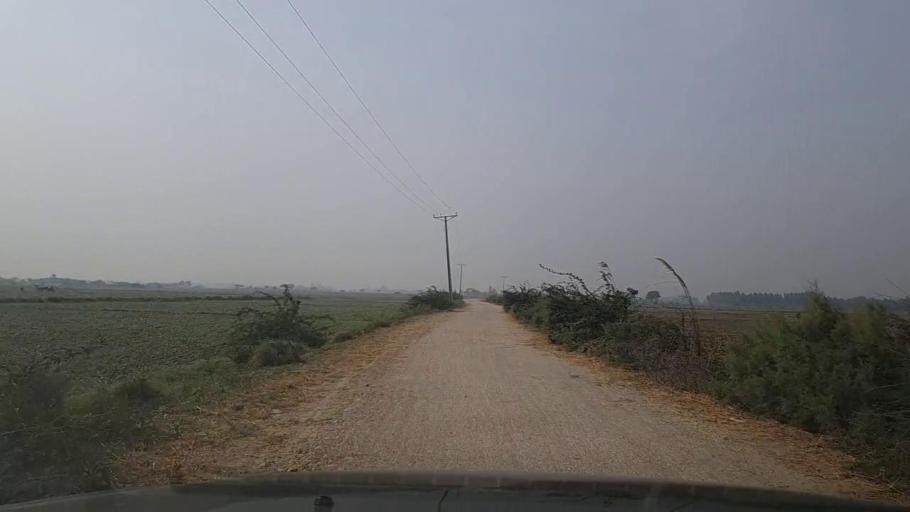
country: PK
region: Sindh
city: Mirpur Sakro
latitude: 24.5467
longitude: 67.8281
